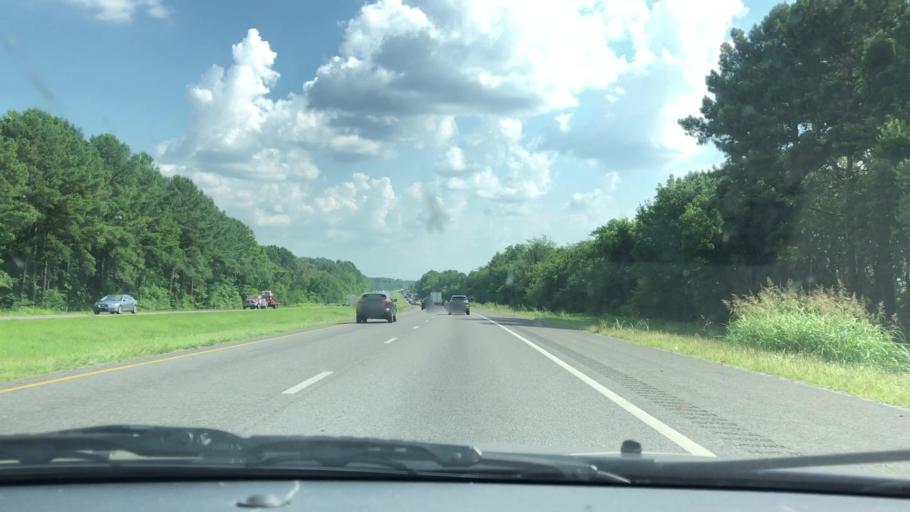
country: US
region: Tennessee
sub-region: Williamson County
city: Thompson's Station
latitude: 35.7813
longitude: -86.8632
